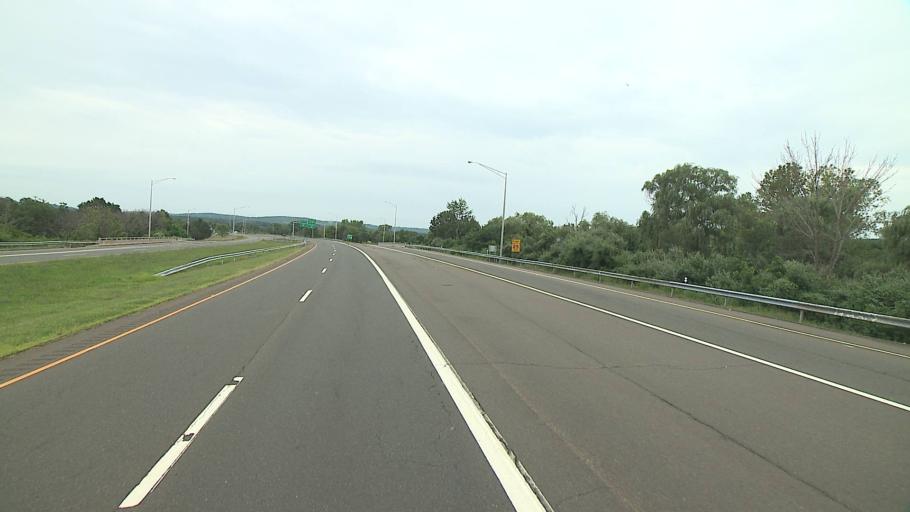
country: US
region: Connecticut
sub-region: New Haven County
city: Hamden
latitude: 41.3816
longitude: -72.8841
